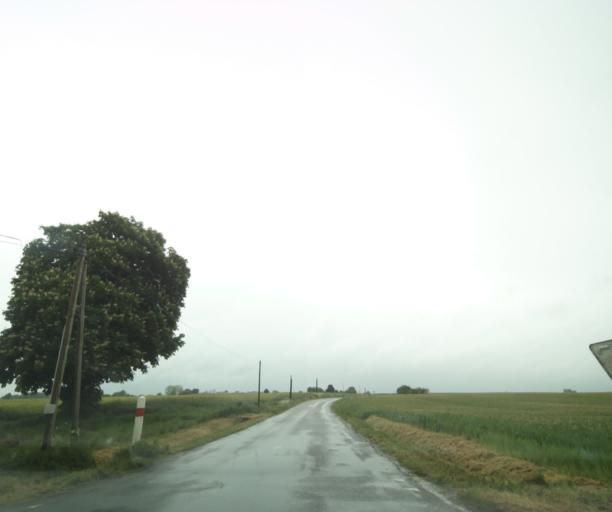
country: FR
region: Poitou-Charentes
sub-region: Departement de la Charente-Maritime
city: Corme-Royal
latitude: 45.7150
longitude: -0.8104
